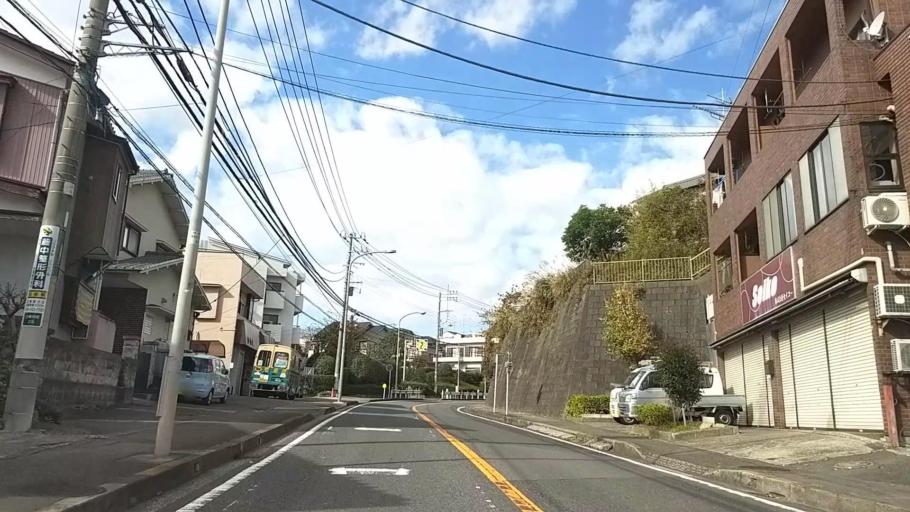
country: JP
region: Kanagawa
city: Yokohama
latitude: 35.4923
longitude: 139.6362
